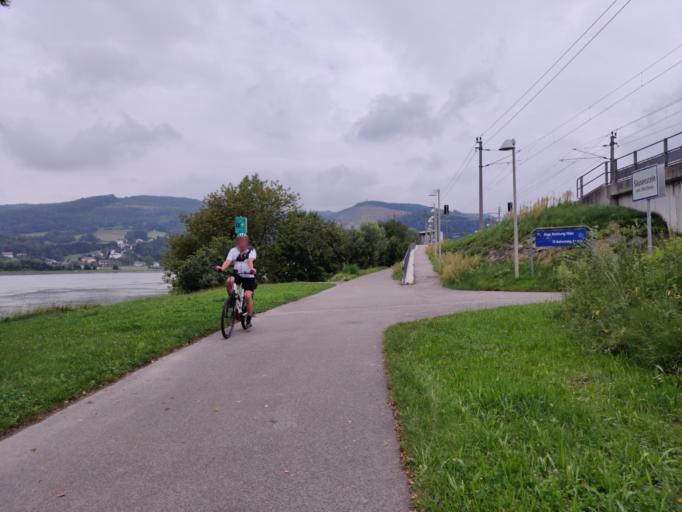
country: AT
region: Lower Austria
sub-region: Politischer Bezirk Melk
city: Ybbs an der Donau
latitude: 48.1920
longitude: 15.1138
